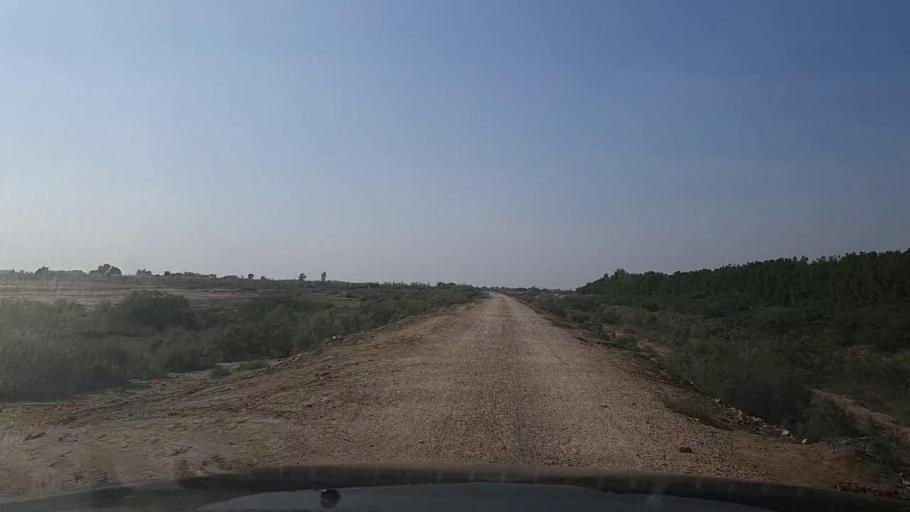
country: PK
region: Sindh
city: Thatta
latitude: 24.7112
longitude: 67.7566
